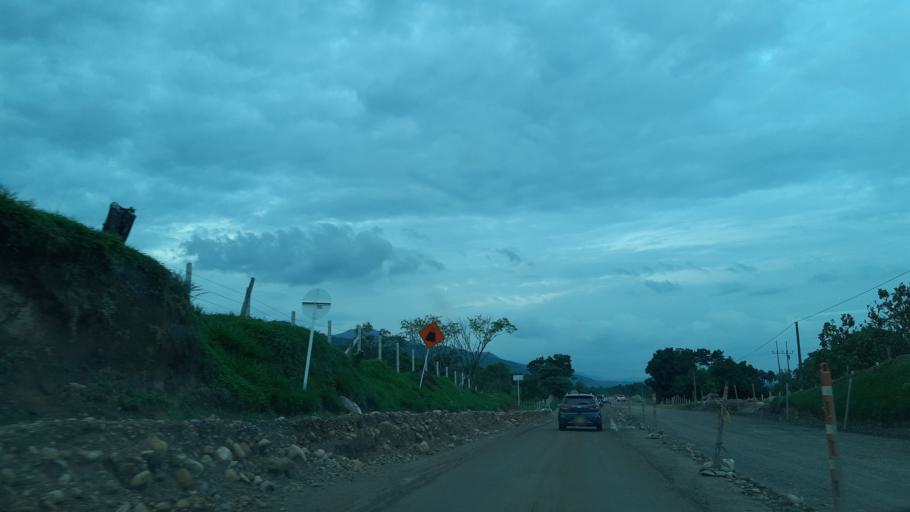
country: CO
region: Casanare
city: Sabanalarga
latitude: 4.7627
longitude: -73.0084
